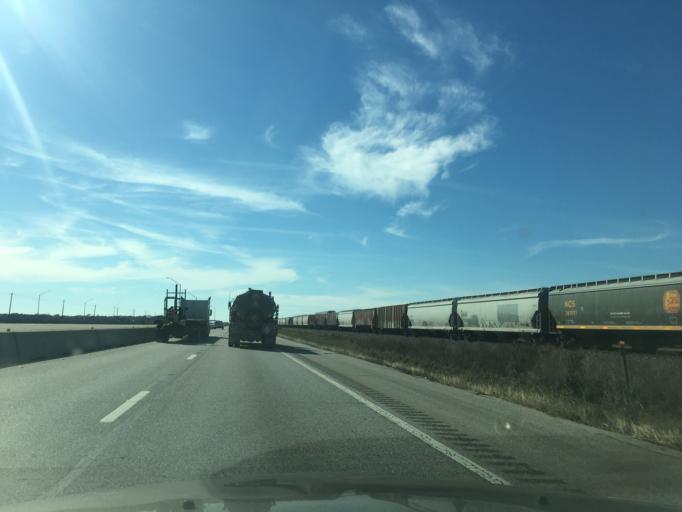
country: US
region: Texas
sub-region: Wharton County
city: East Bernard
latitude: 29.4756
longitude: -95.9535
